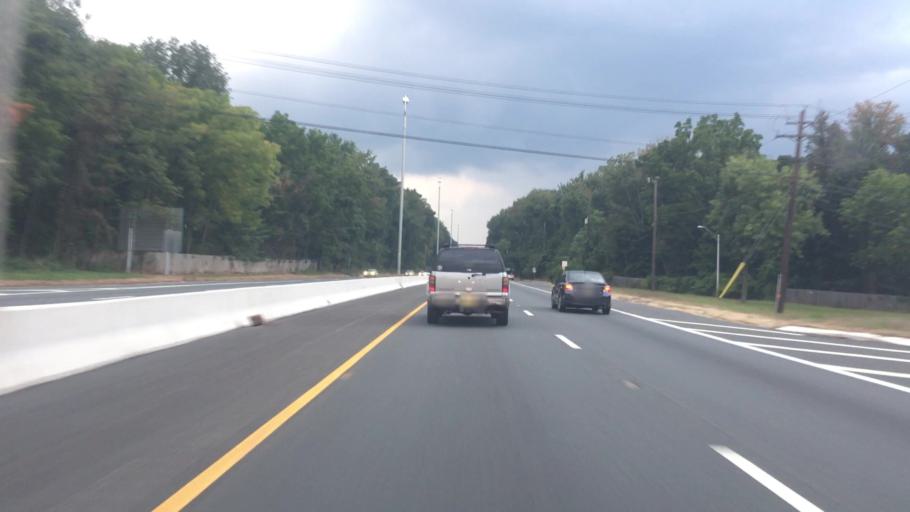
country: US
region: New Jersey
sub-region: Bergen County
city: Wyckoff
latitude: 40.9978
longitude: -74.1808
